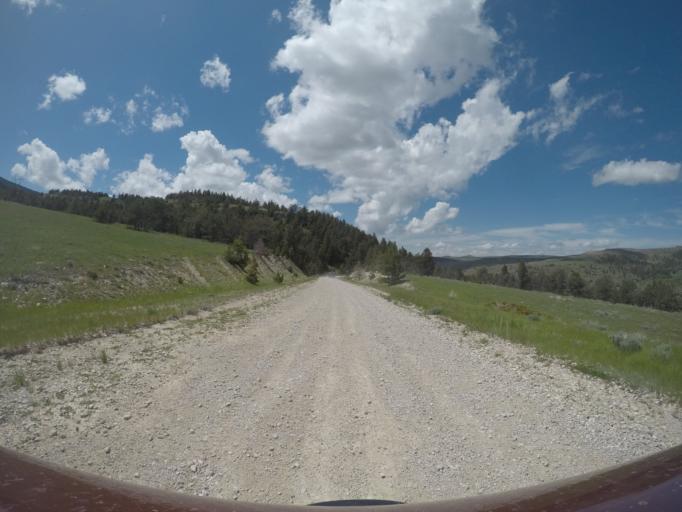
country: US
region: Wyoming
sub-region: Big Horn County
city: Lovell
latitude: 45.2061
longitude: -108.5400
